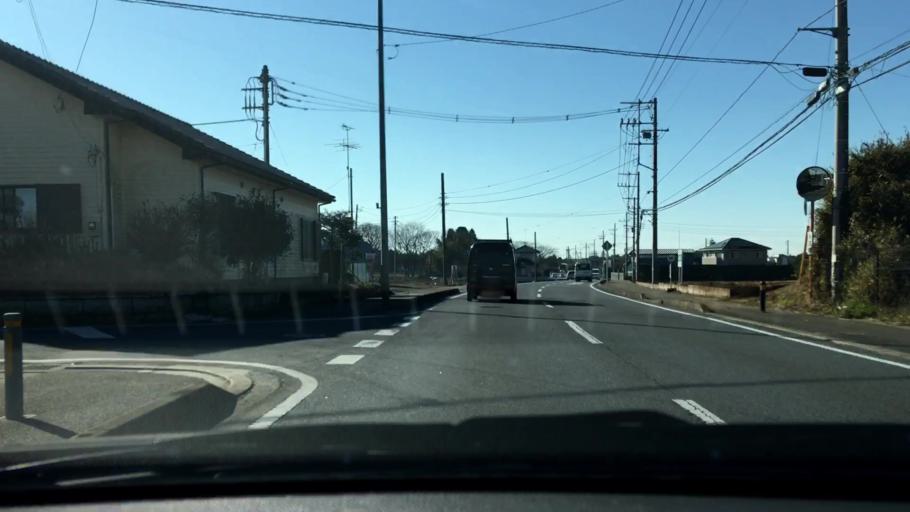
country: JP
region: Chiba
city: Narita
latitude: 35.7255
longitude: 140.3343
